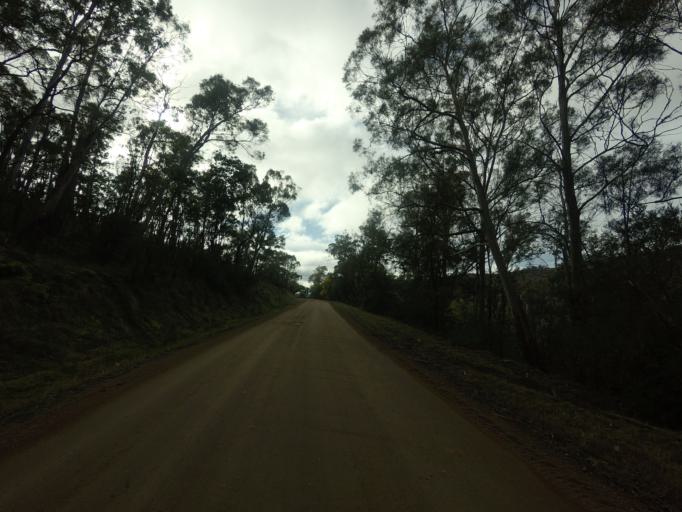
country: AU
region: Tasmania
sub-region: Derwent Valley
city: New Norfolk
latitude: -42.7396
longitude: 146.8694
